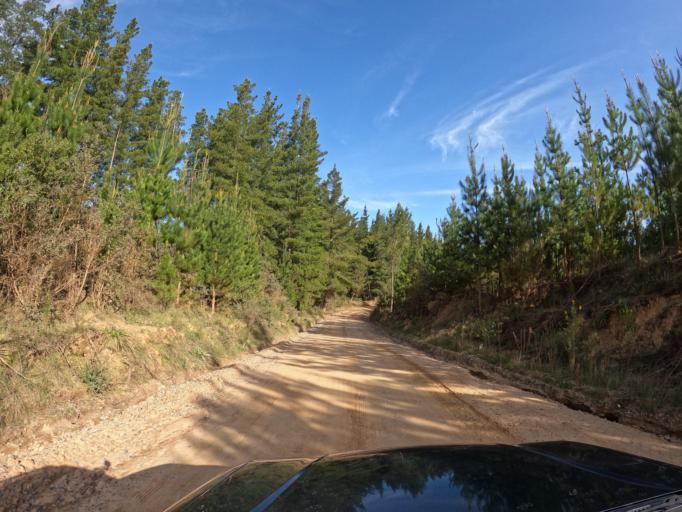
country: CL
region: Biobio
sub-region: Provincia de Biobio
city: Yumbel
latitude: -37.1019
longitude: -72.7412
